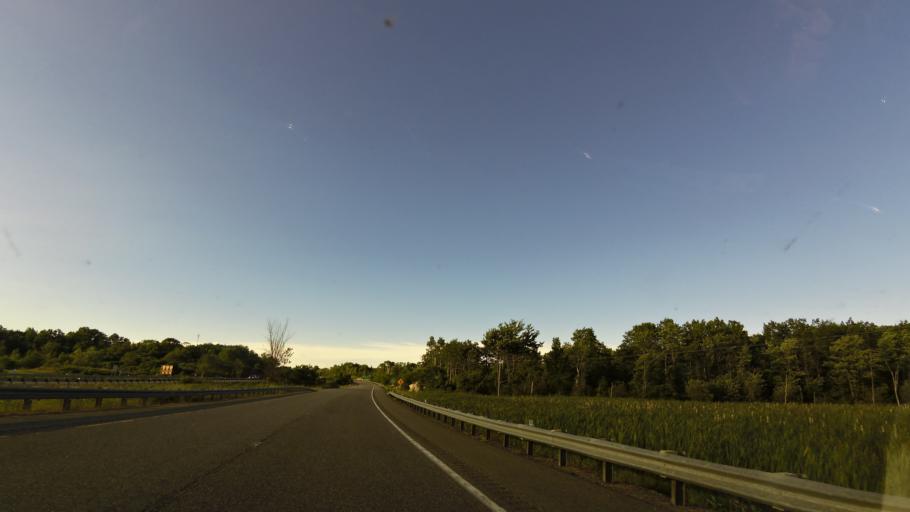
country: CA
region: Ontario
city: Midland
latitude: 44.8410
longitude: -79.7382
